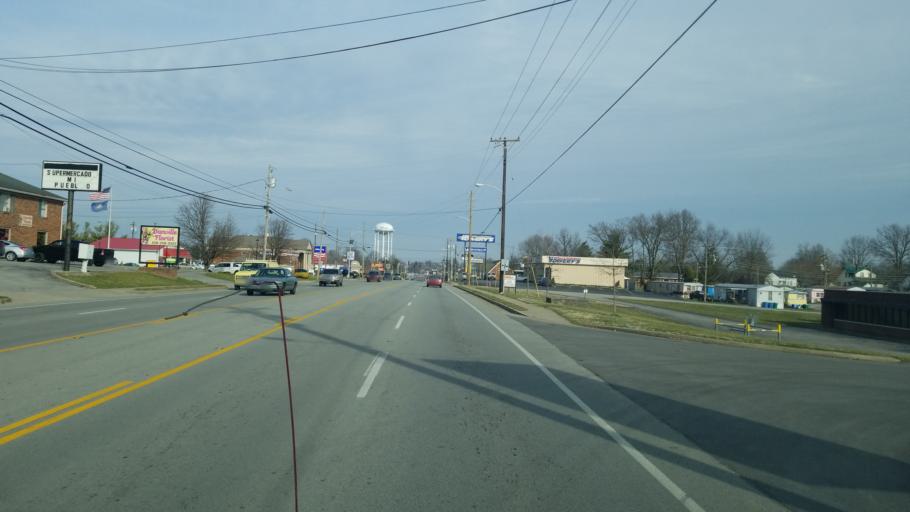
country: US
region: Kentucky
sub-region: Boyle County
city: Danville
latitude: 37.6263
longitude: -84.7747
